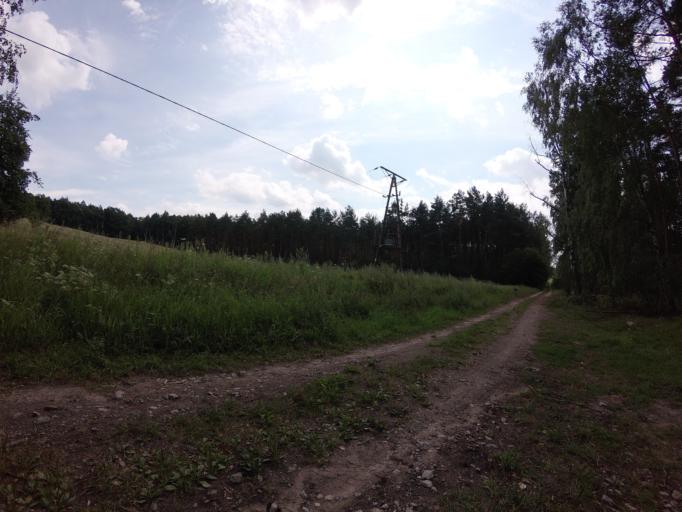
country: PL
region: Kujawsko-Pomorskie
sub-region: Powiat bydgoski
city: Koronowo
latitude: 53.3795
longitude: 17.9757
